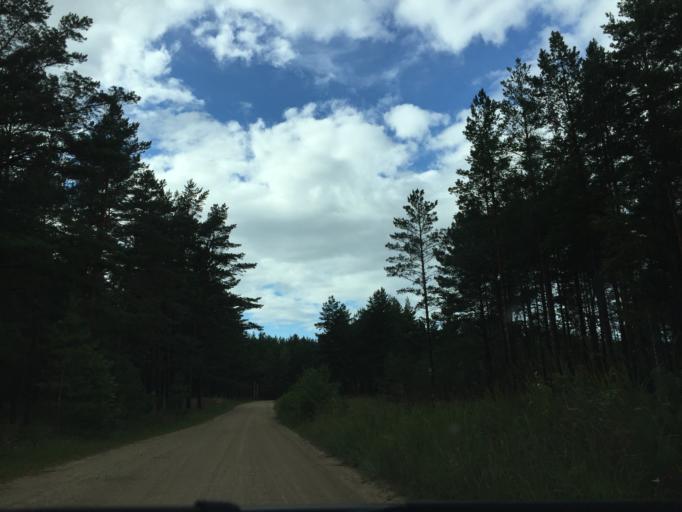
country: LV
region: Saulkrastu
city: Saulkrasti
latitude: 57.1720
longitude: 24.3817
